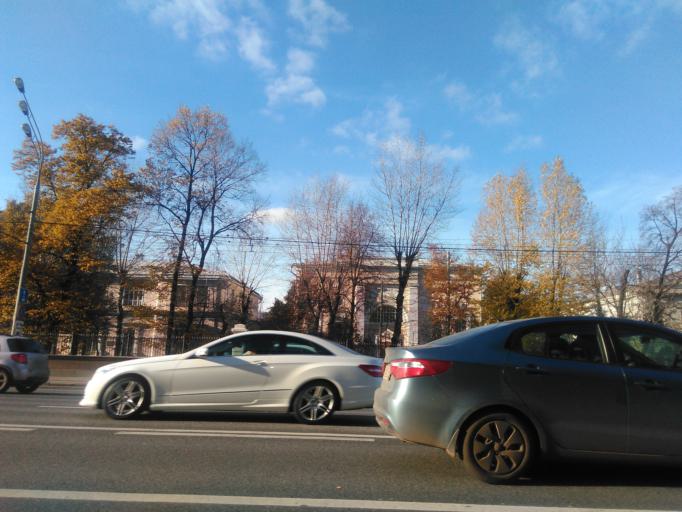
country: RU
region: Moscow
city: Moscow
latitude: 55.7237
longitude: 37.6036
